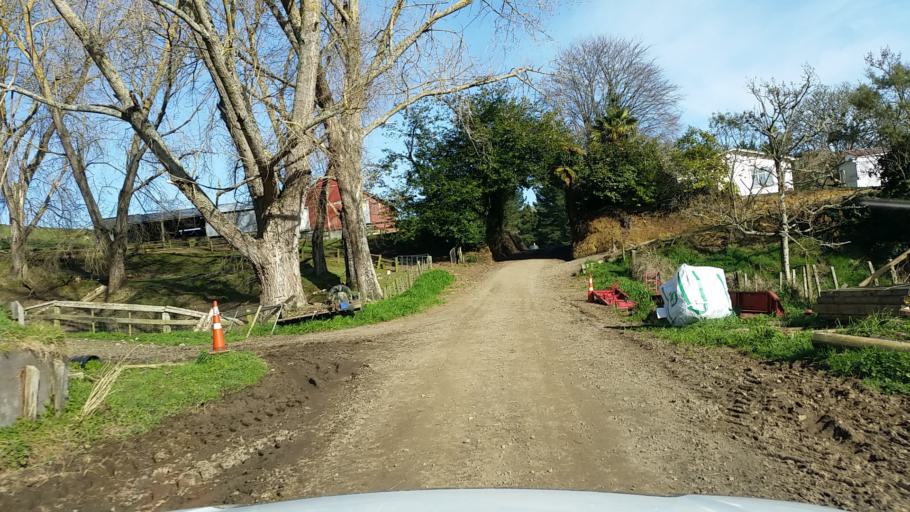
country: NZ
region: Taranaki
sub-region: South Taranaki District
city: Eltham
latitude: -39.3188
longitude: 174.5320
